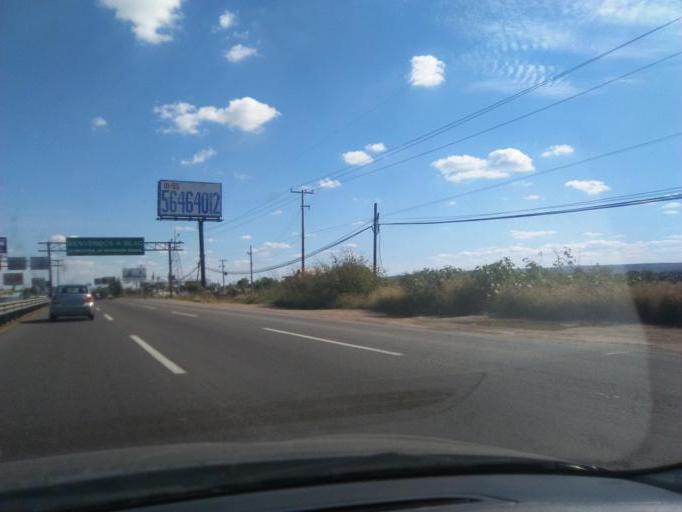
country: MX
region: Guanajuato
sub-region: Silao de la Victoria
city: El Refugio de los Sauces
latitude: 21.0207
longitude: -101.5344
